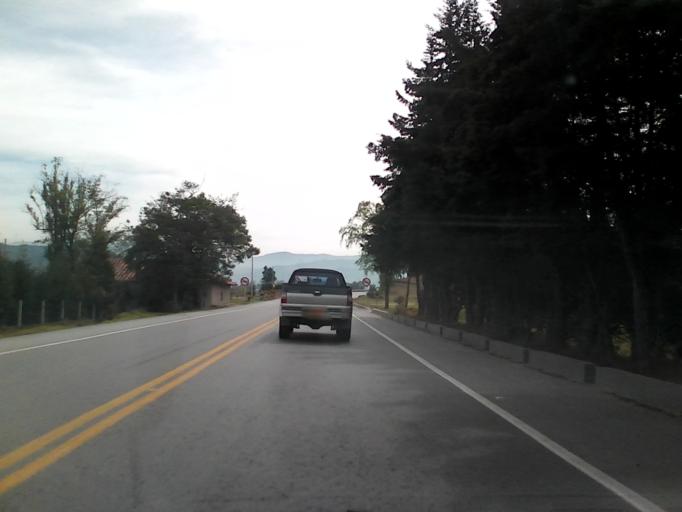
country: CO
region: Boyaca
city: Tibasosa
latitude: 5.7438
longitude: -72.9814
